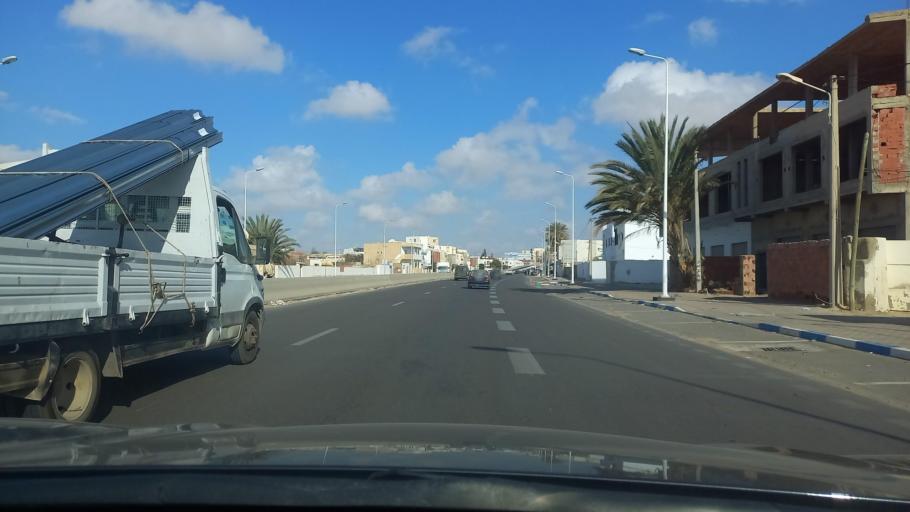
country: TN
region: Safaqis
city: Sfax
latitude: 34.7409
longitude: 10.7240
